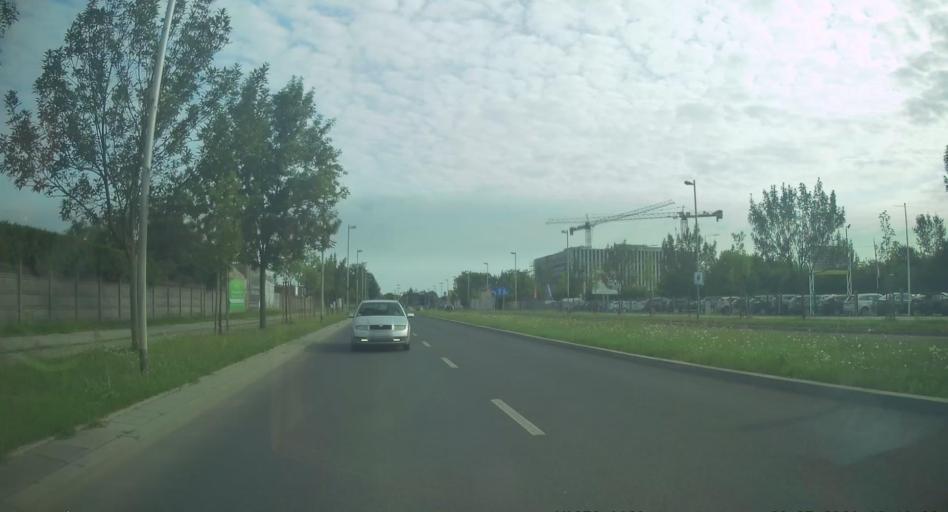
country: PL
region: Silesian Voivodeship
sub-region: Czestochowa
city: Czestochowa
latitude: 50.8221
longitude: 19.0884
